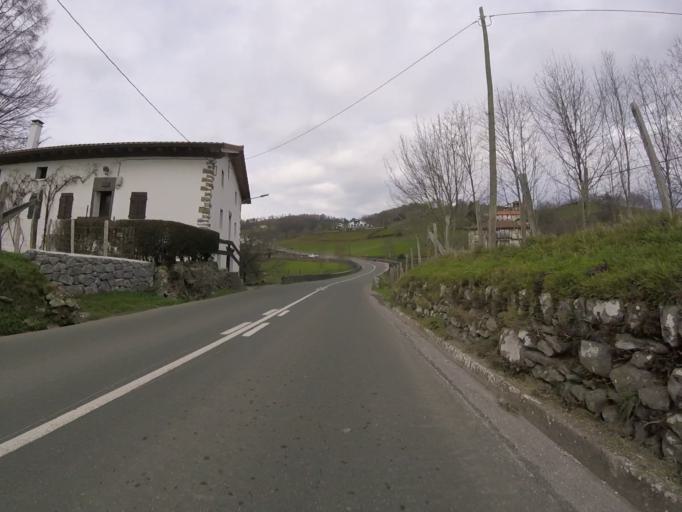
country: ES
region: Basque Country
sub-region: Provincia de Guipuzcoa
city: Errezil
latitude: 43.1406
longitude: -2.1634
